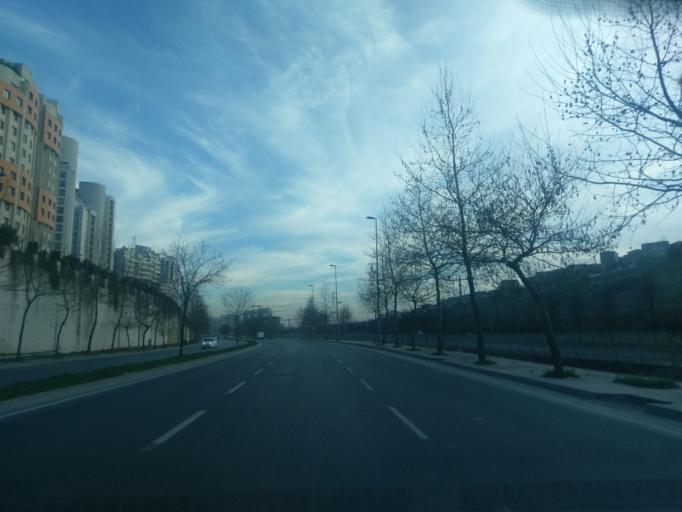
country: TR
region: Istanbul
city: Basaksehir
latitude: 41.0494
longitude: 28.7577
